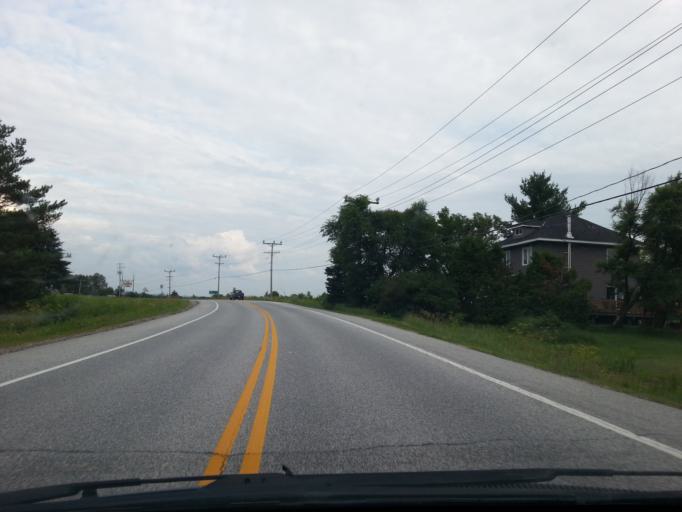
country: CA
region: Quebec
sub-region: Outaouais
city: Wakefield
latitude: 45.8645
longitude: -76.0212
